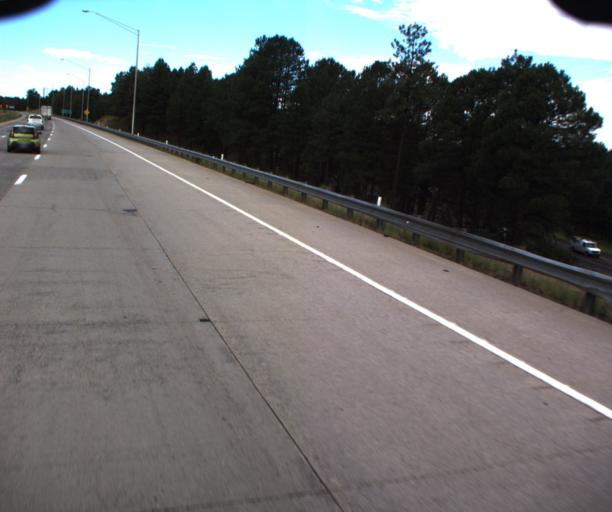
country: US
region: Arizona
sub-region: Coconino County
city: Flagstaff
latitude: 35.1645
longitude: -111.6727
